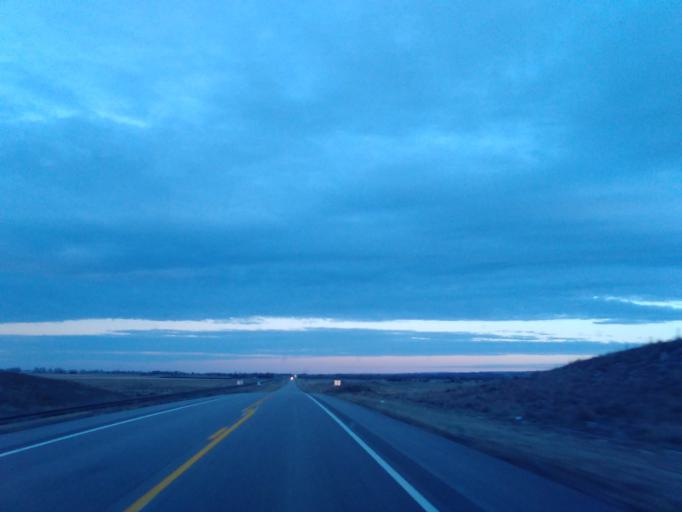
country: US
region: Nebraska
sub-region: Garden County
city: Oshkosh
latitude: 41.3733
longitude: -102.2512
